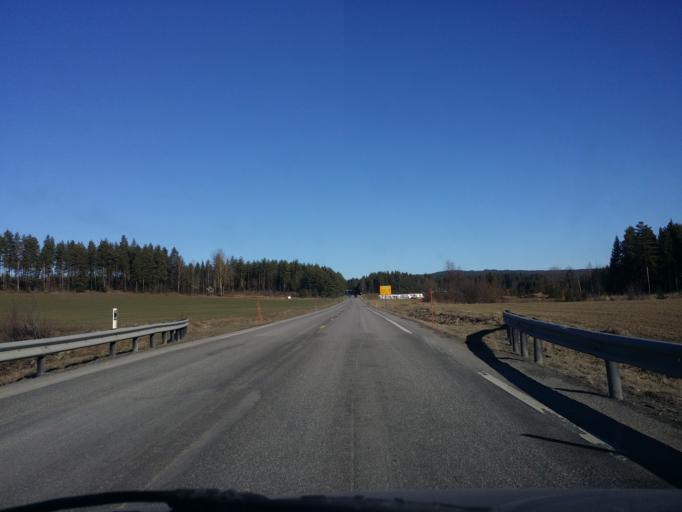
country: NO
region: Buskerud
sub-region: Ringerike
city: Honefoss
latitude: 60.2116
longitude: 10.2569
